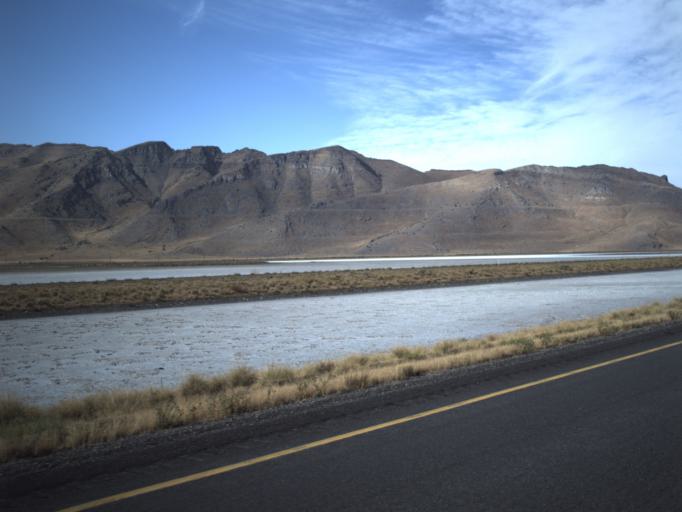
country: US
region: Utah
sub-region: Tooele County
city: Grantsville
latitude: 40.7268
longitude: -112.5761
